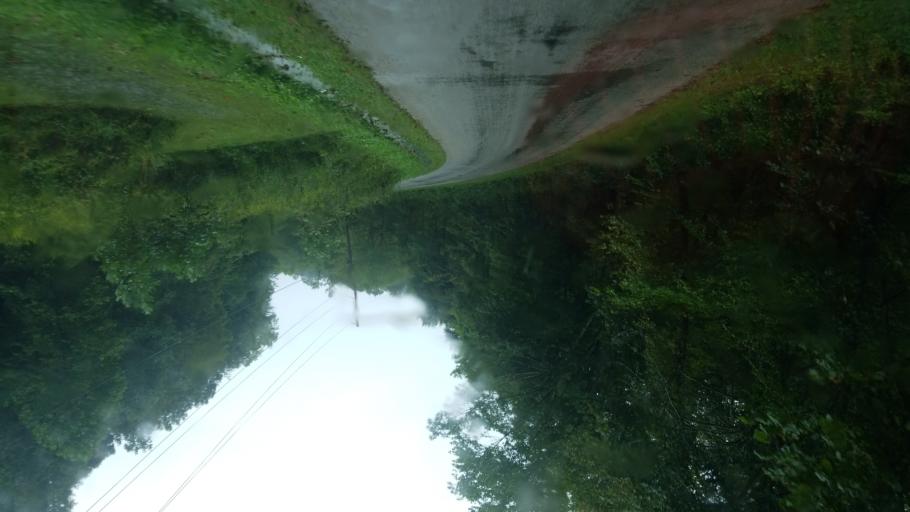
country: US
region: Ohio
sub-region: Adams County
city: Peebles
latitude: 38.8043
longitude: -83.2498
